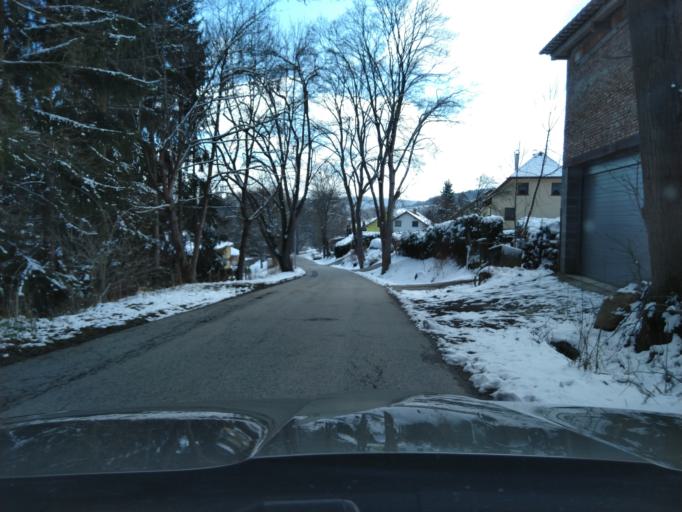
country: CZ
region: Jihocesky
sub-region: Okres Prachatice
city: Vimperk
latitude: 49.0567
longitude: 13.7635
